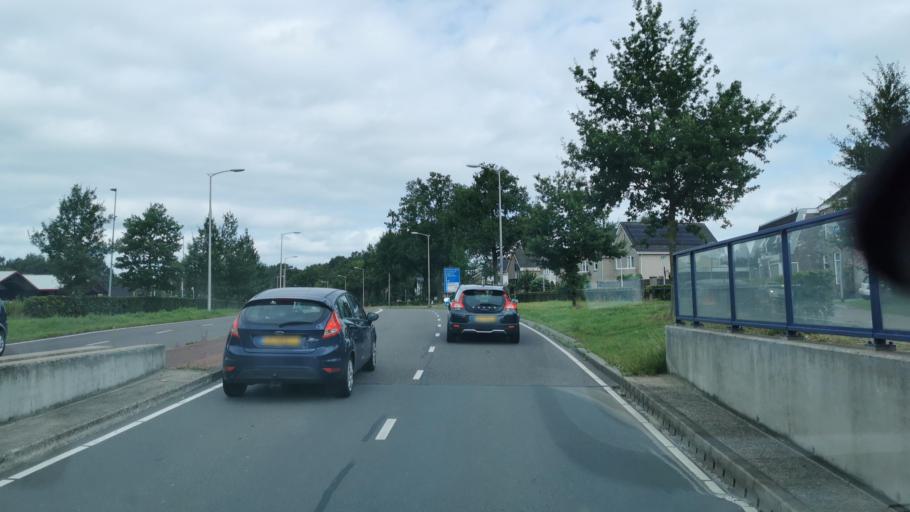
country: NL
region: Overijssel
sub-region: Gemeente Oldenzaal
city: Oldenzaal
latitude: 52.3042
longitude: 6.9217
